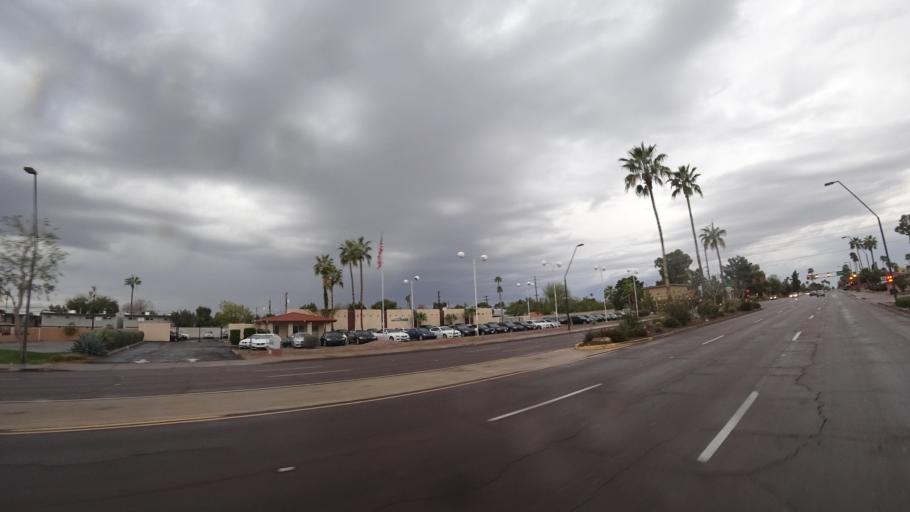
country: US
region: Arizona
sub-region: Maricopa County
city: Tempe
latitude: 33.4499
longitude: -111.9264
